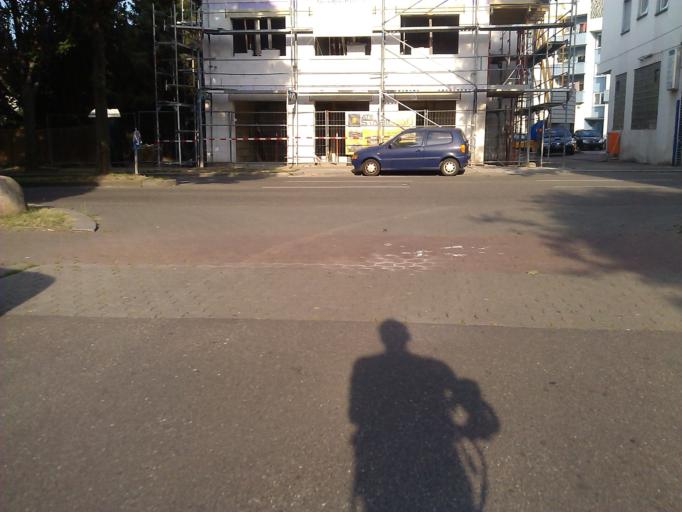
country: DE
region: Baden-Wuerttemberg
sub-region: Regierungsbezirk Stuttgart
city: Heilbronn
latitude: 49.1299
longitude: 9.2112
